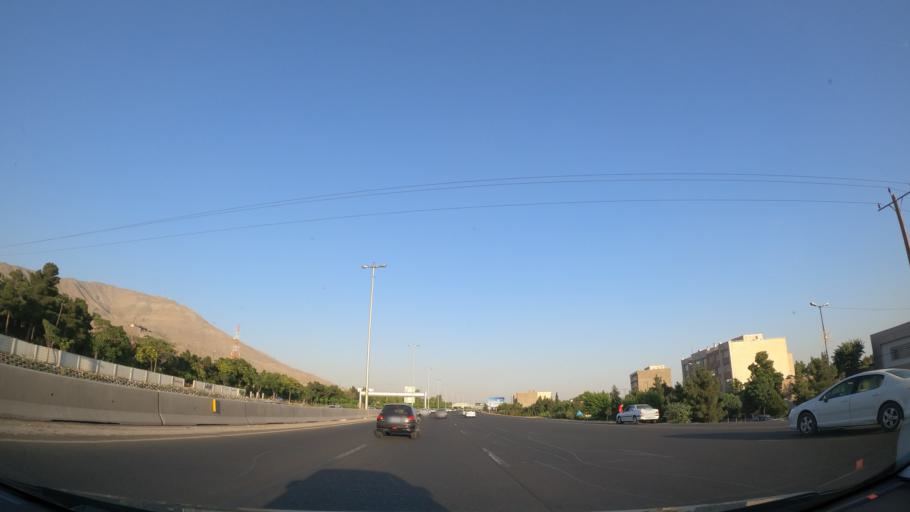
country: IR
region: Alborz
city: Karaj
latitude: 35.7860
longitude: 51.0257
